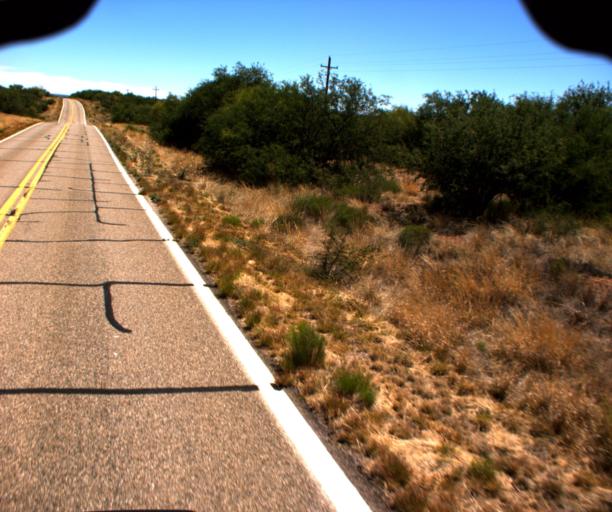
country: US
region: Arizona
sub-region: Pima County
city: Three Points
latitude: 31.7095
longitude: -111.4878
